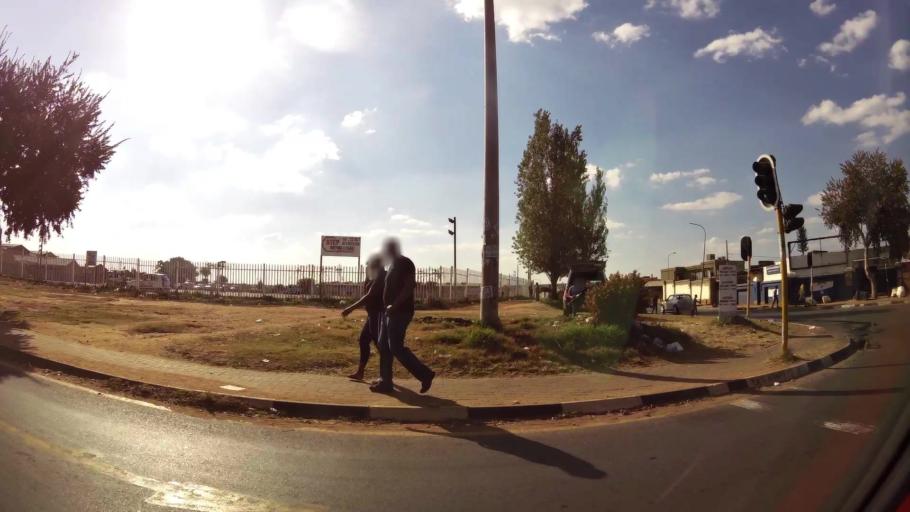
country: ZA
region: Gauteng
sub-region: City of Johannesburg Metropolitan Municipality
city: Roodepoort
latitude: -26.2143
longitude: 27.8759
